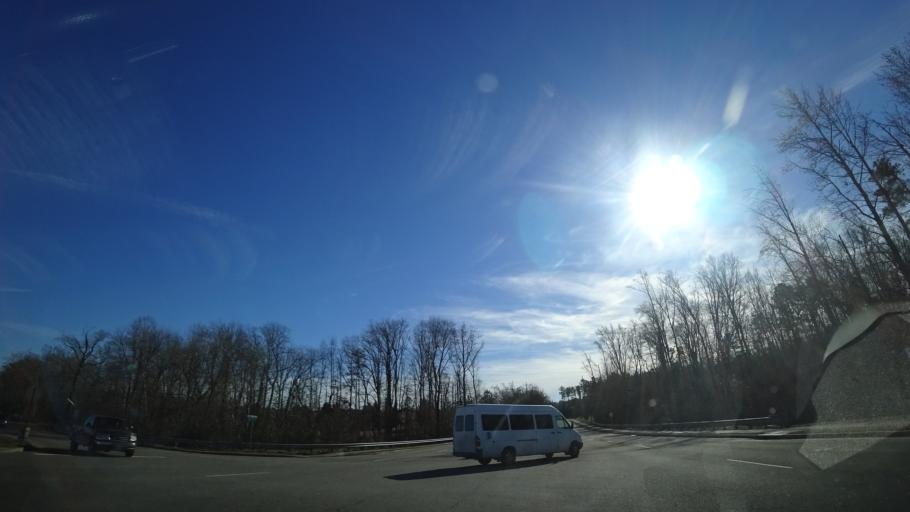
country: US
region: Virginia
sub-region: Hanover County
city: Ashland
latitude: 37.7572
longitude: -77.4635
